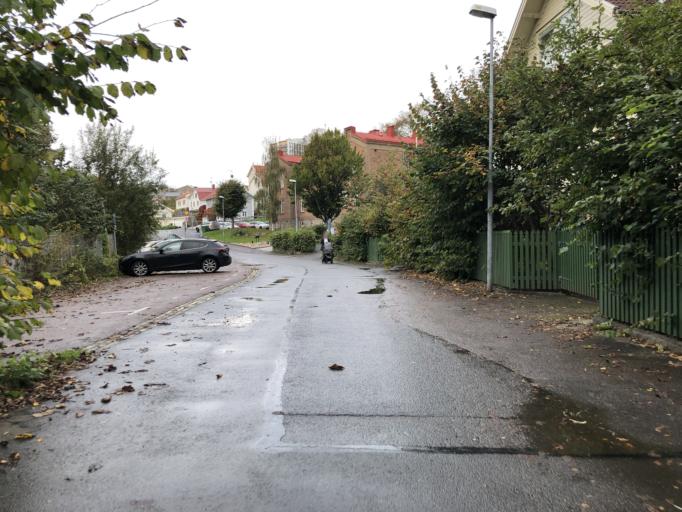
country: SE
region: Vaestra Goetaland
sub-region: Molndal
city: Moelndal
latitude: 57.6544
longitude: 12.0286
